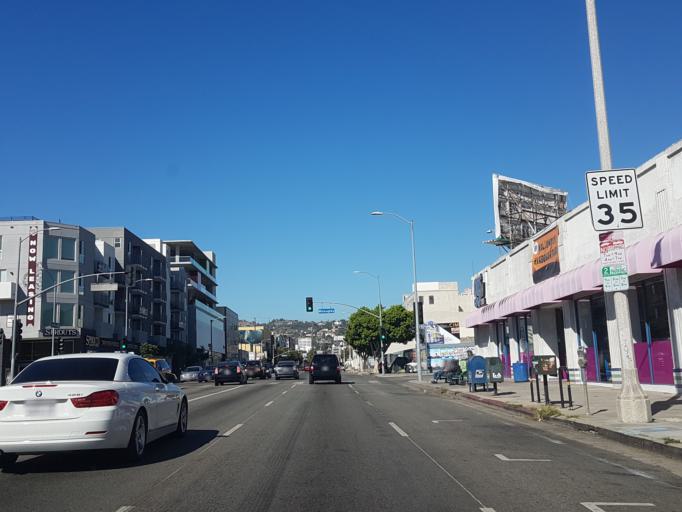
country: US
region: California
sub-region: Los Angeles County
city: West Hollywood
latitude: 34.0866
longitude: -118.3440
